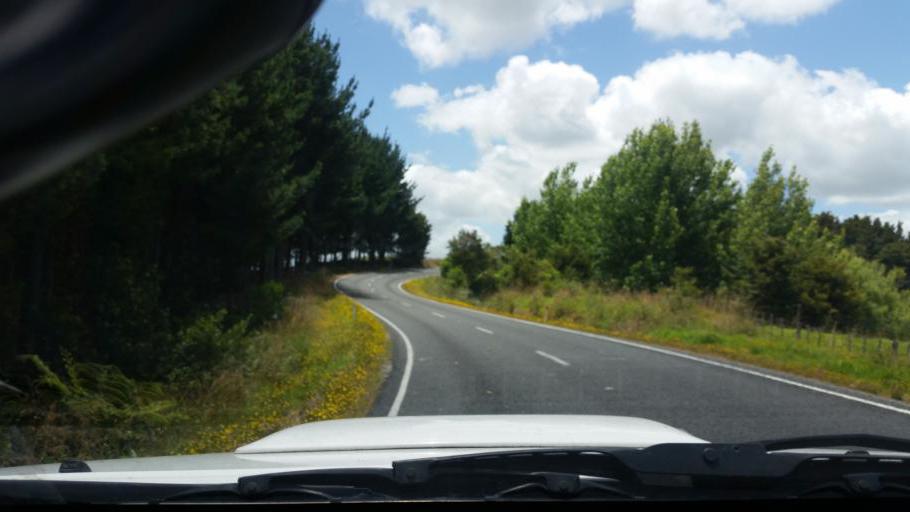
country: NZ
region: Northland
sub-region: Whangarei
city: Ruakaka
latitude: -36.0494
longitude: 174.2756
